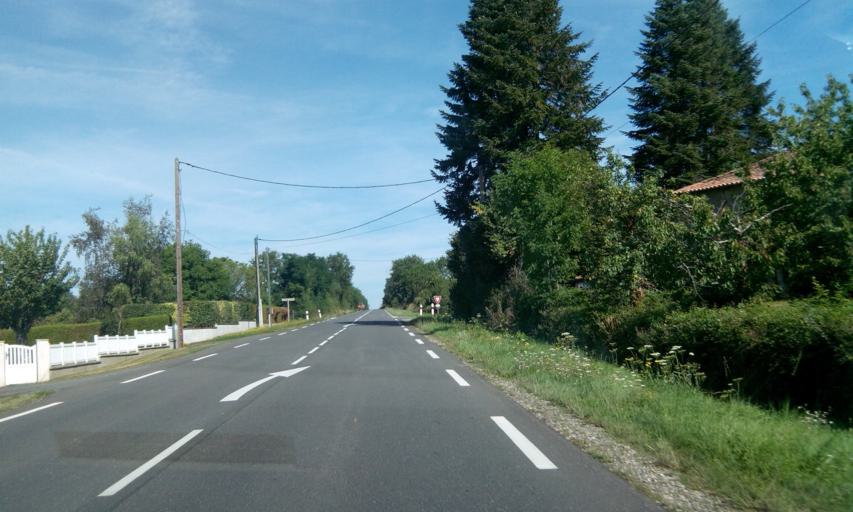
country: FR
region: Poitou-Charentes
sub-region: Departement de la Charente
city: Etagnac
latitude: 45.9408
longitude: 0.7297
